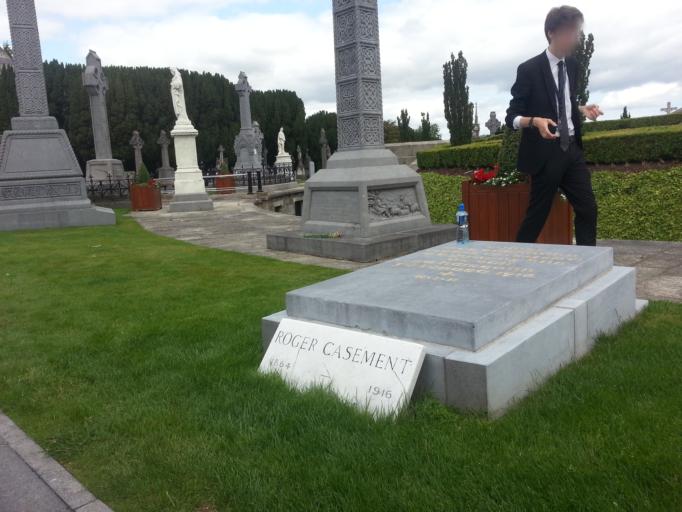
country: IE
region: Leinster
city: Glasnevin
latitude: 53.3700
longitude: -6.2774
